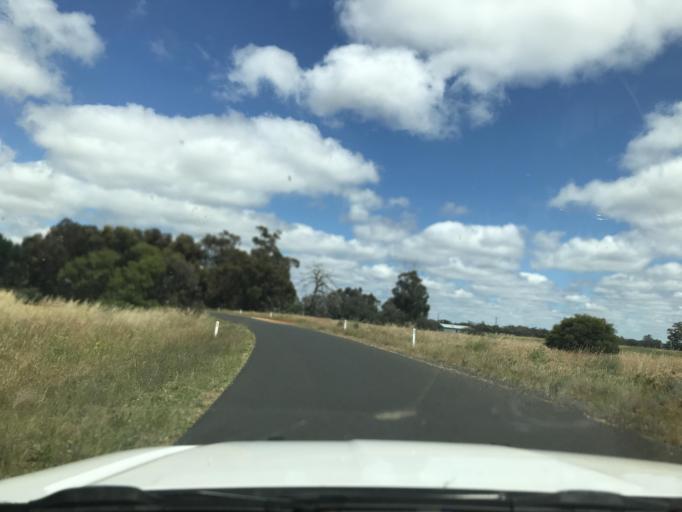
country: AU
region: South Australia
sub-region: Naracoorte and Lucindale
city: Naracoorte
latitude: -36.6674
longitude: 141.2840
